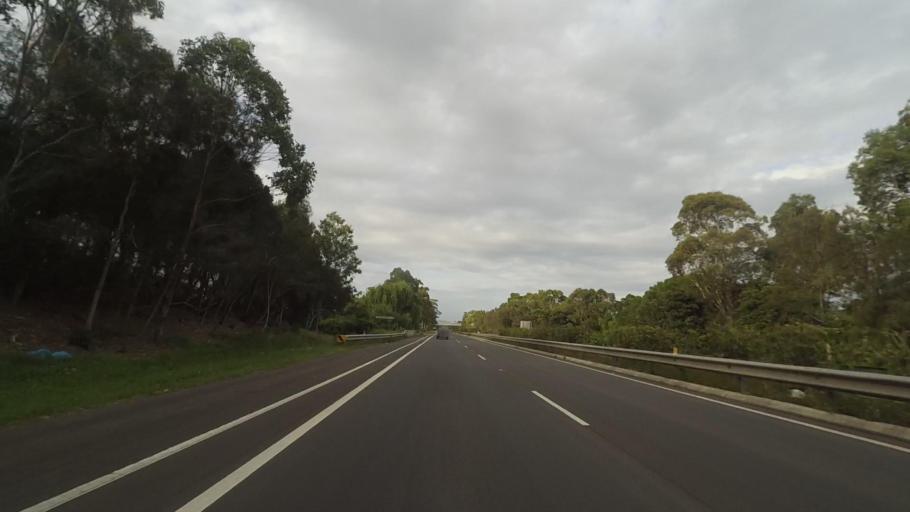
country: AU
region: New South Wales
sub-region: Wollongong
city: Fairy Meadow
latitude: -34.3989
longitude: 150.8941
